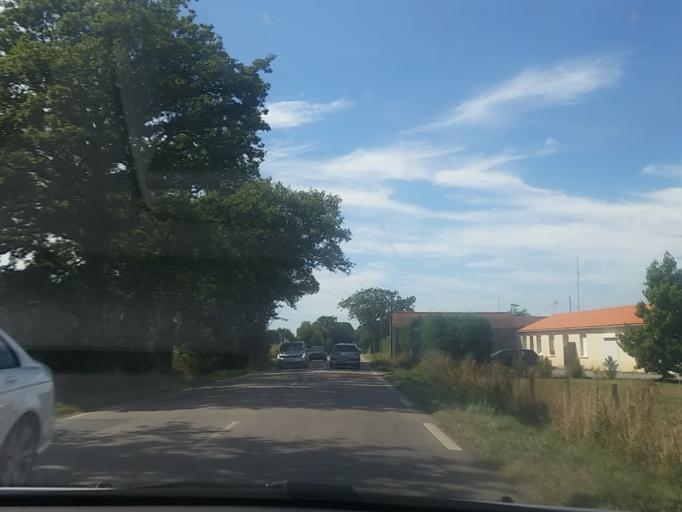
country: FR
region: Pays de la Loire
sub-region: Departement de la Loire-Atlantique
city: Saint-Pere-en-Retz
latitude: 47.1919
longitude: -2.0218
